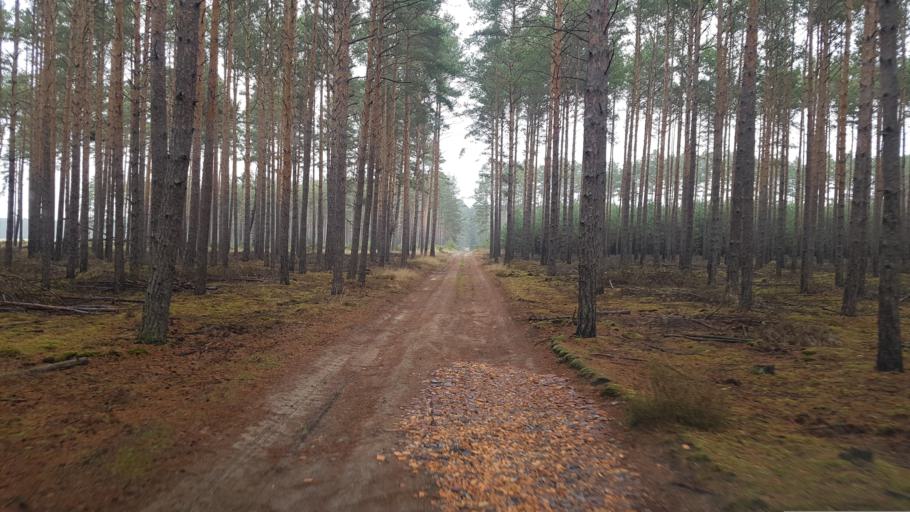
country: DE
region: Brandenburg
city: Sallgast
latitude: 51.6492
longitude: 13.8173
